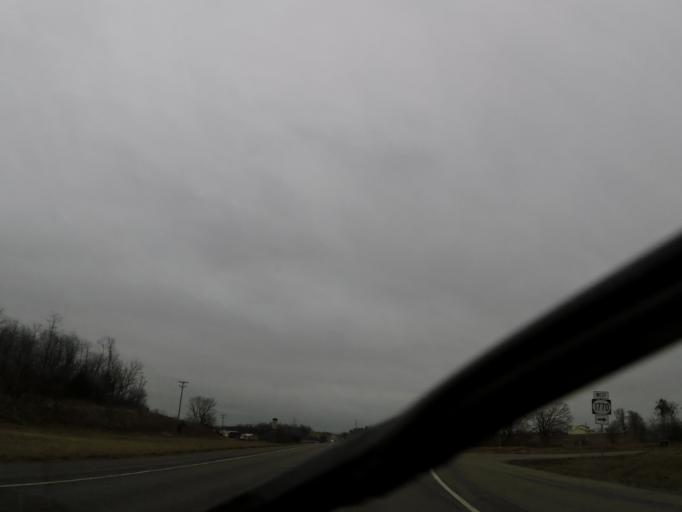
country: US
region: Kentucky
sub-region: Lincoln County
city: Stanford
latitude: 37.5187
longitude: -84.6136
